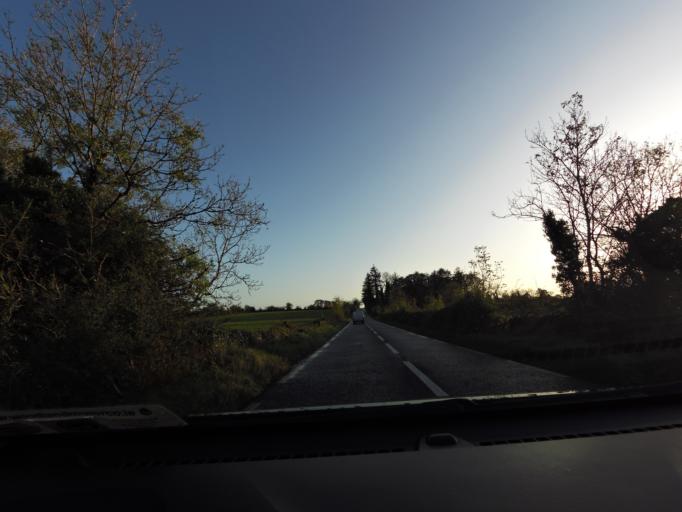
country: IE
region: Connaught
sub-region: Roscommon
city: Castlerea
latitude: 53.7278
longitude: -8.5557
